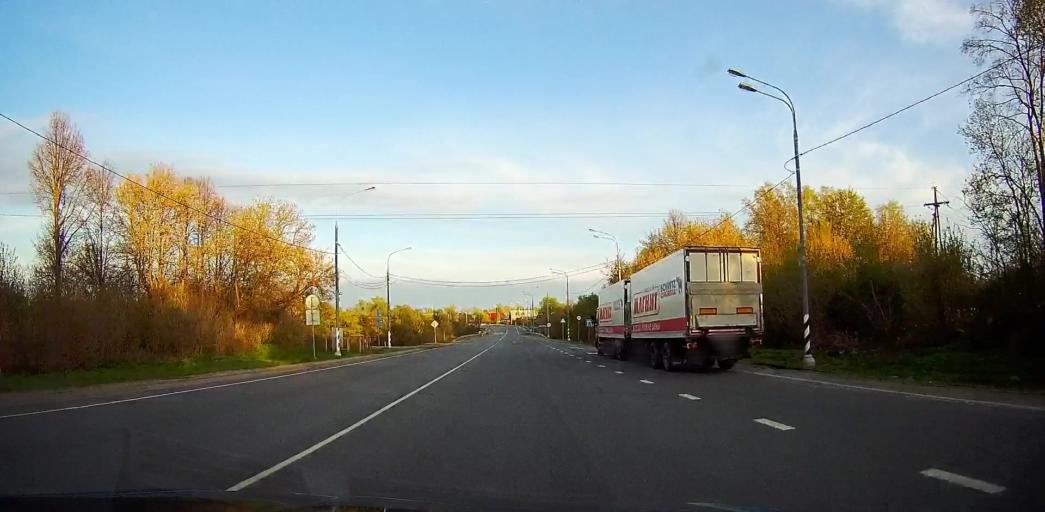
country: RU
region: Moskovskaya
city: Troitskoye
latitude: 55.2279
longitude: 38.5575
